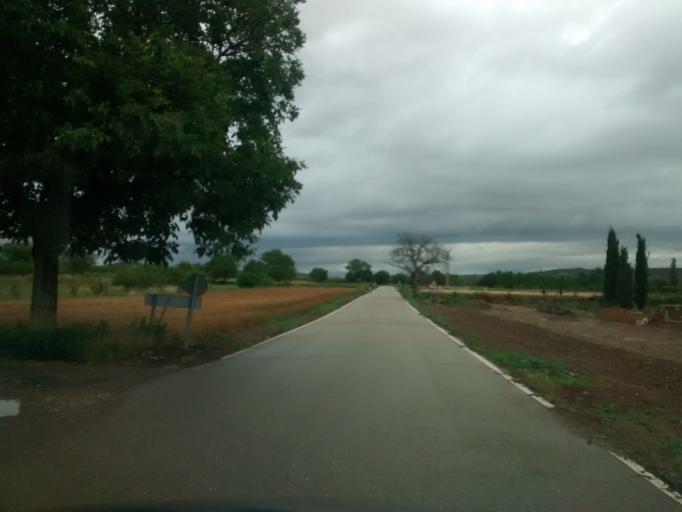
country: ES
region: Aragon
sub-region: Provincia de Zaragoza
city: Vera de Moncayo
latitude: 41.8244
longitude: -1.6899
